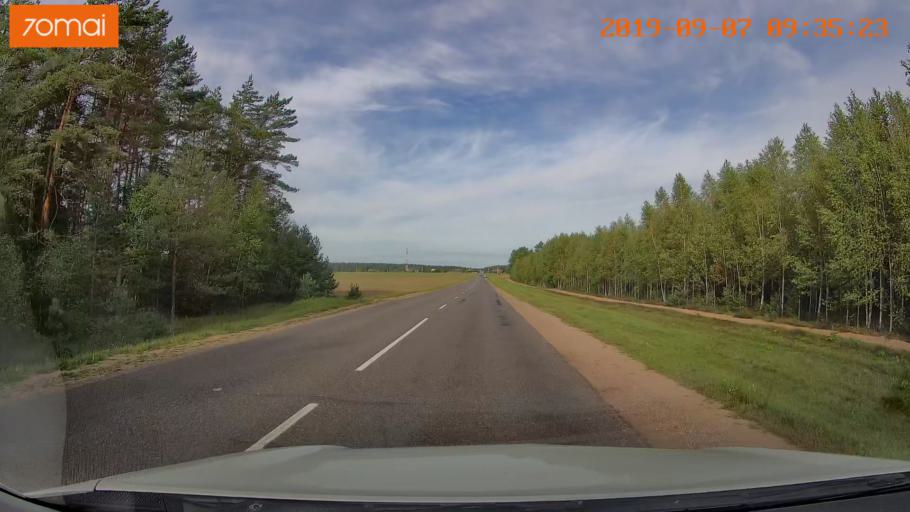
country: BY
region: Grodnenskaya
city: Iwye
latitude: 53.9113
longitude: 25.8710
